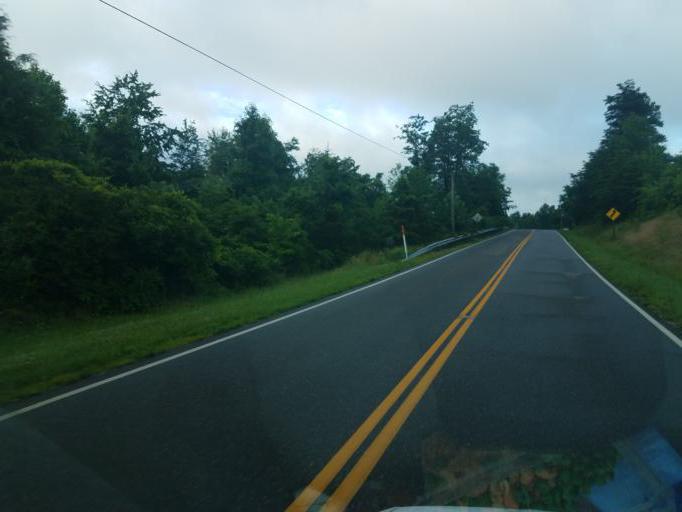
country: US
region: Ohio
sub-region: Gallia County
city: Gallipolis
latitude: 38.8721
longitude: -82.3794
